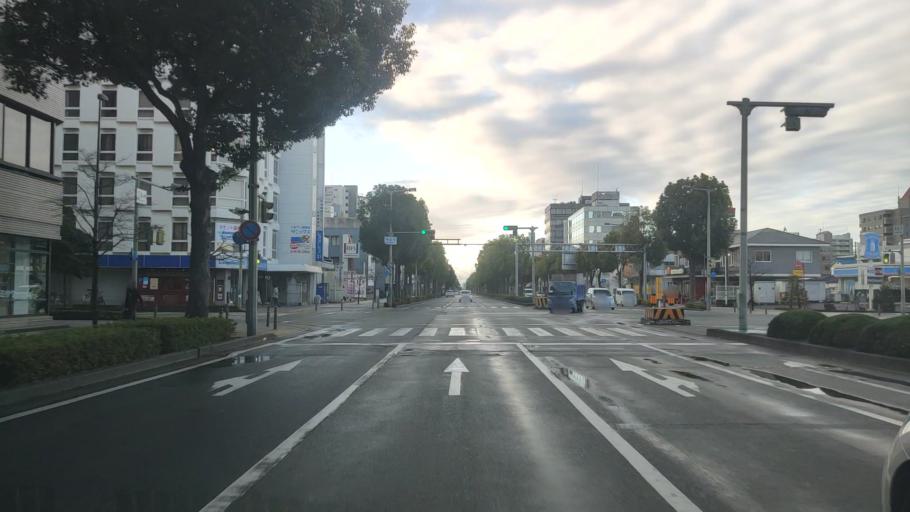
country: JP
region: Hyogo
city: Himeji
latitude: 34.8219
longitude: 134.6874
